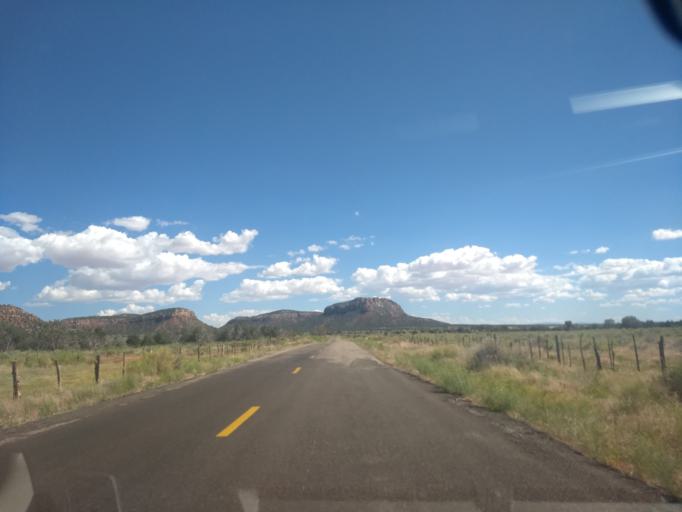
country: US
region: Utah
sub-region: Washington County
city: Hildale
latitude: 36.9547
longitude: -112.8746
